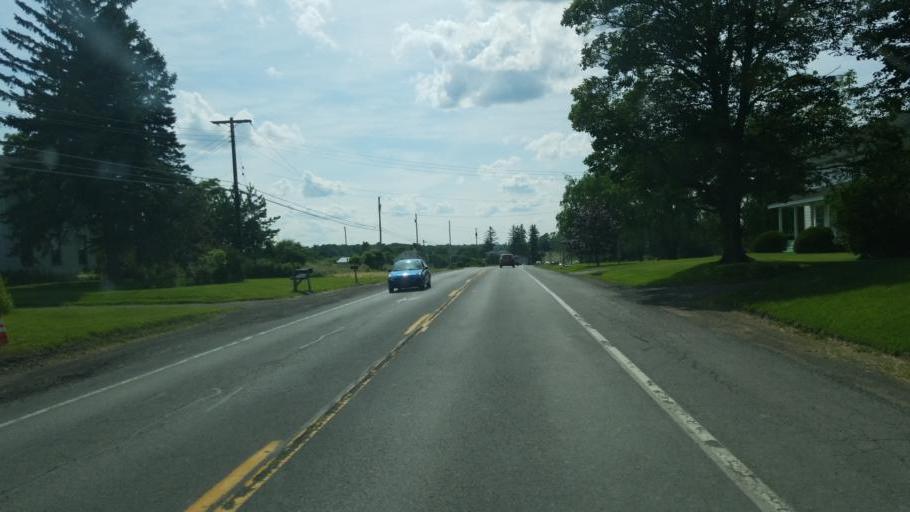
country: US
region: New York
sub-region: Ontario County
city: Clifton Springs
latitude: 42.8606
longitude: -77.1663
